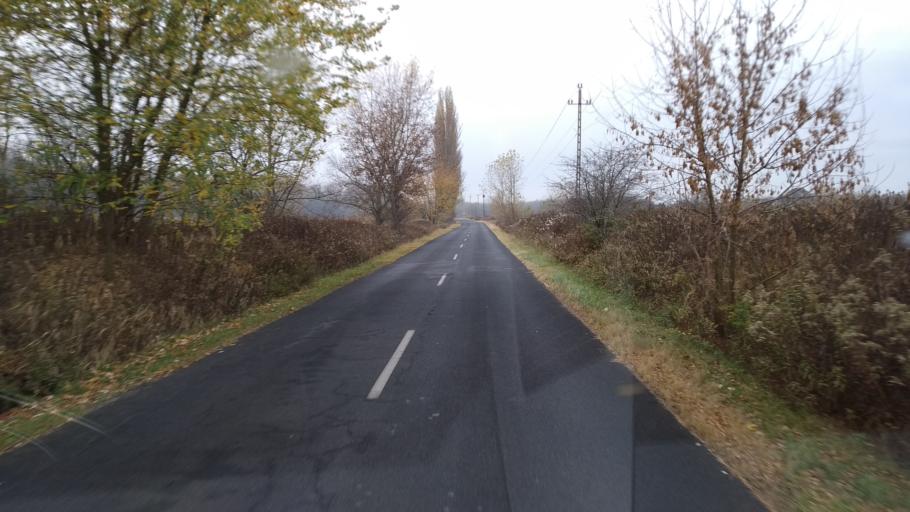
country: HU
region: Pest
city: Dunabogdany
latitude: 47.7907
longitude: 19.0818
